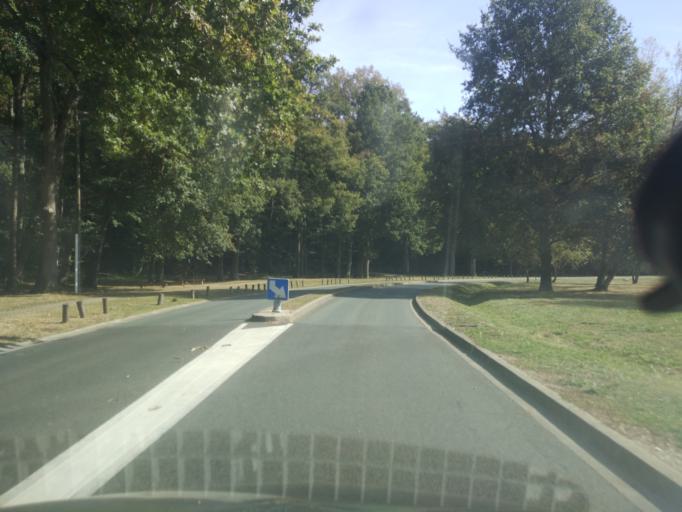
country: FR
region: Ile-de-France
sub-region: Departement de l'Essonne
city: Limours
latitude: 48.6455
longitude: 2.0884
